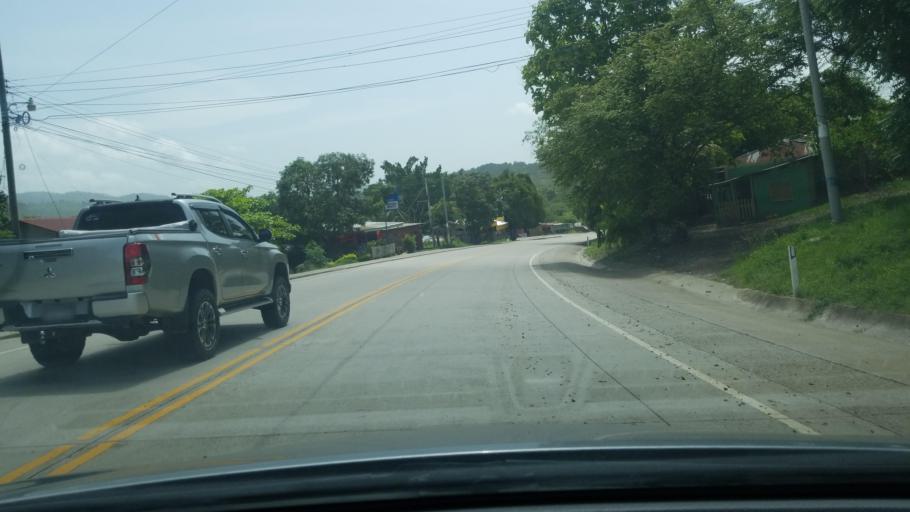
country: HN
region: Copan
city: Florida
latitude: 15.0649
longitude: -88.7909
